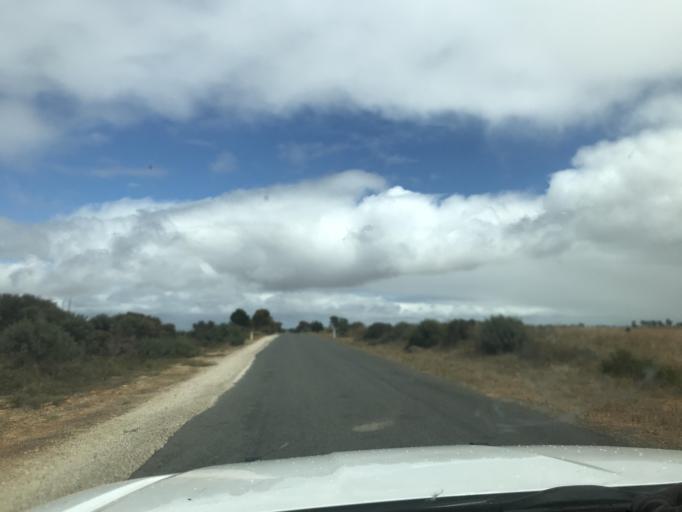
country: AU
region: South Australia
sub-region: Tatiara
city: Bordertown
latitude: -36.1391
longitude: 141.2159
